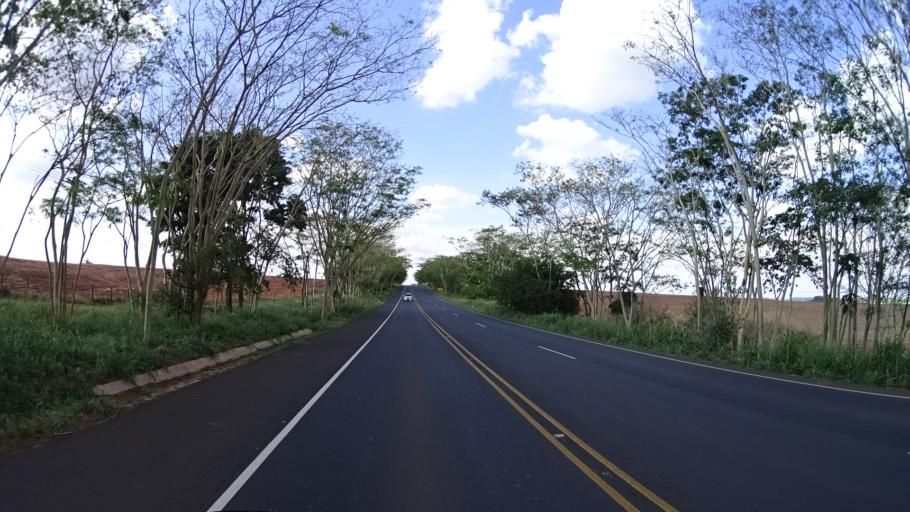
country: BR
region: Sao Paulo
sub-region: Urupes
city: Urupes
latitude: -21.0401
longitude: -49.2429
